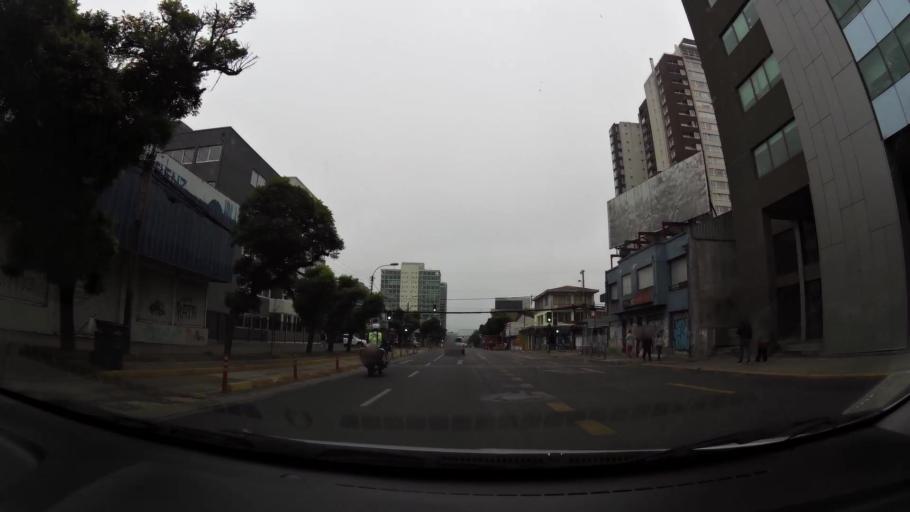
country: CL
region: Biobio
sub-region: Provincia de Concepcion
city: Concepcion
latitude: -36.8297
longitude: -73.0551
